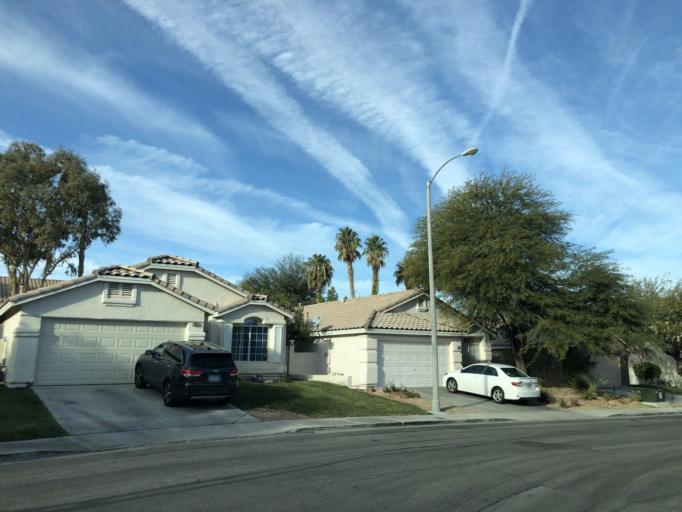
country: US
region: Nevada
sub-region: Clark County
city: Whitney
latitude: 36.0204
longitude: -115.0729
